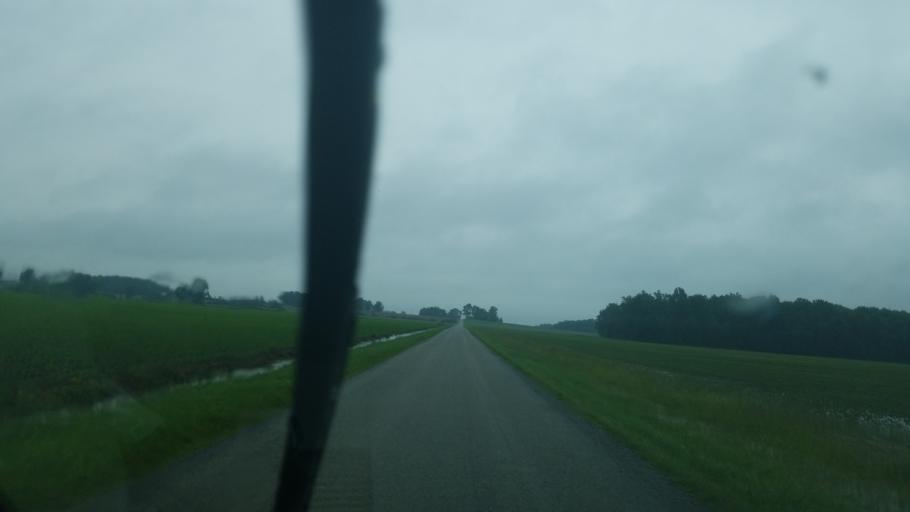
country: US
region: Ohio
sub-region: Huron County
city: Willard
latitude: 40.9350
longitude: -82.7974
